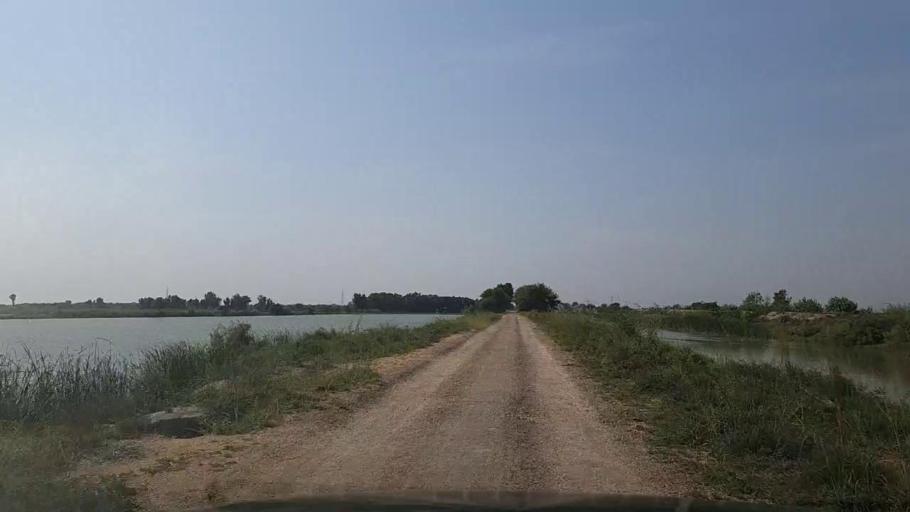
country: PK
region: Sindh
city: Thatta
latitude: 24.8061
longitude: 67.8567
